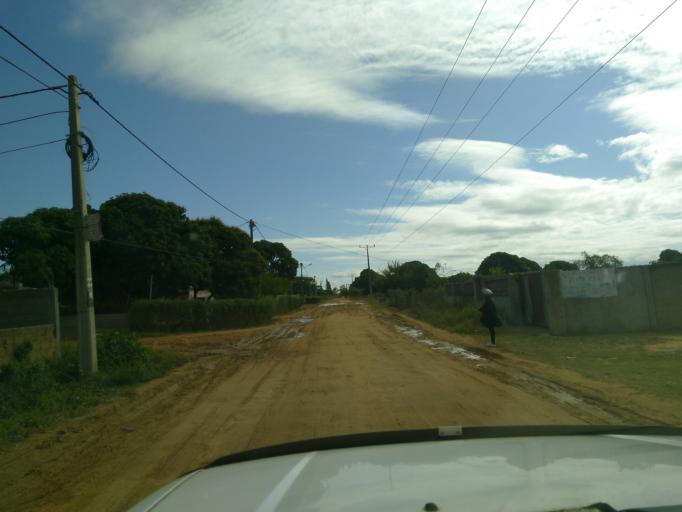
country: MZ
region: Maputo City
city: Maputo
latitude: -25.9964
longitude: 32.5387
